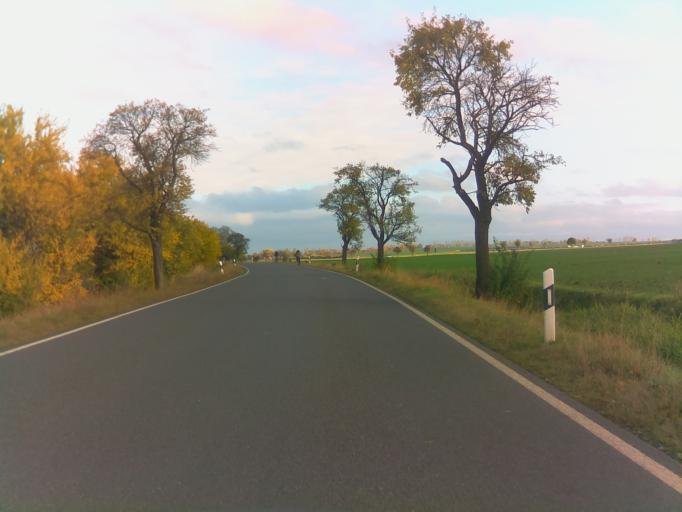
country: DE
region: Thuringia
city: Bosleben-Wullersleben
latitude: 50.8468
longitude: 11.0526
